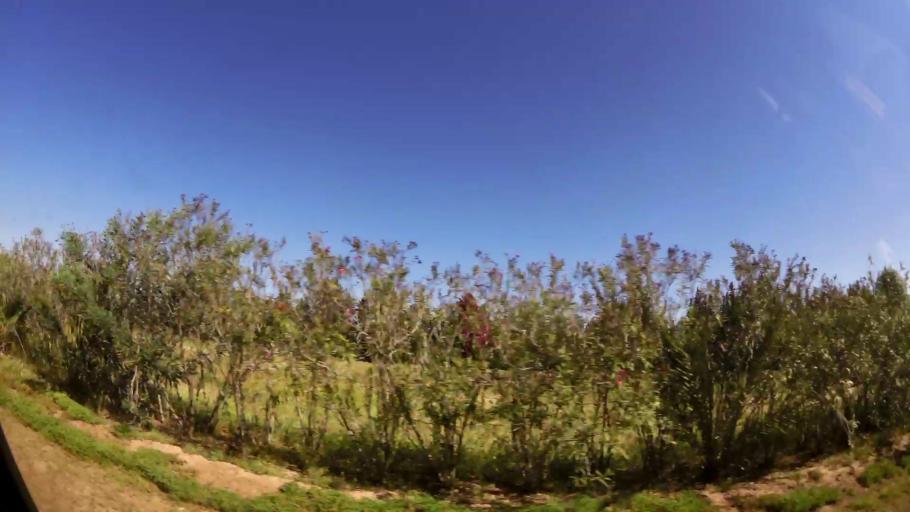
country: MA
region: Marrakech-Tensift-Al Haouz
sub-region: Marrakech
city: Marrakesh
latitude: 31.6628
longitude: -7.9381
